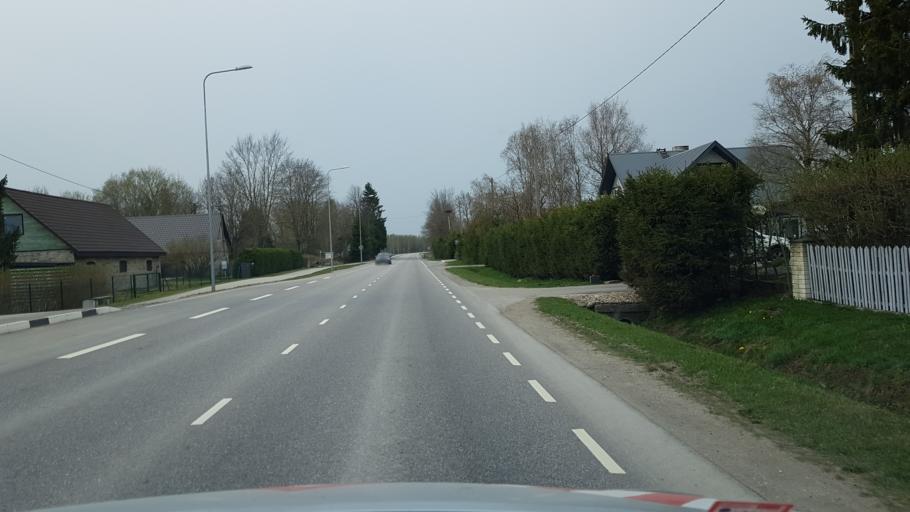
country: EE
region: Harju
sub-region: Joelaehtme vald
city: Loo
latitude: 59.4033
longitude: 24.9400
